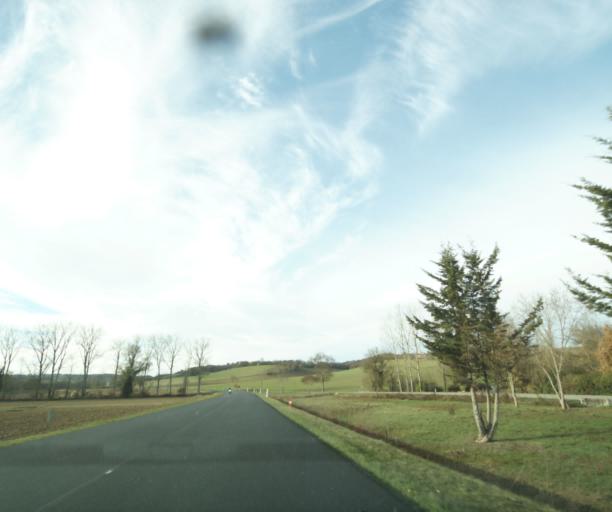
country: FR
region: Midi-Pyrenees
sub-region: Departement du Gers
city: Jegun
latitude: 43.6899
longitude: 0.4791
